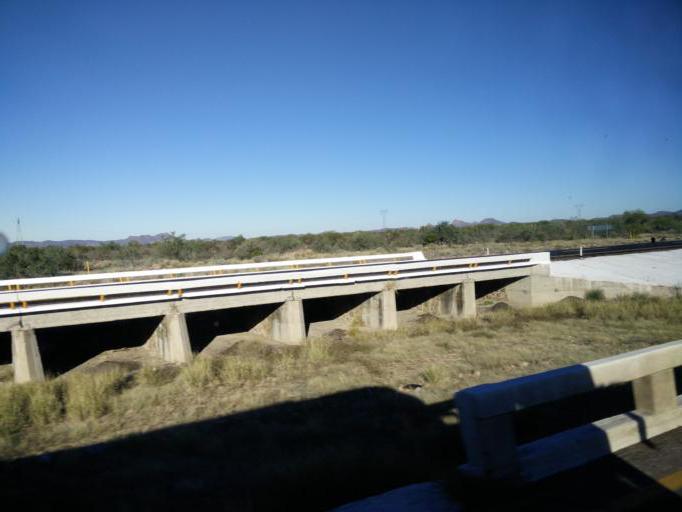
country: MX
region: Sonora
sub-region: Empalme
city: Empalme
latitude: 28.3669
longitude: -111.0428
